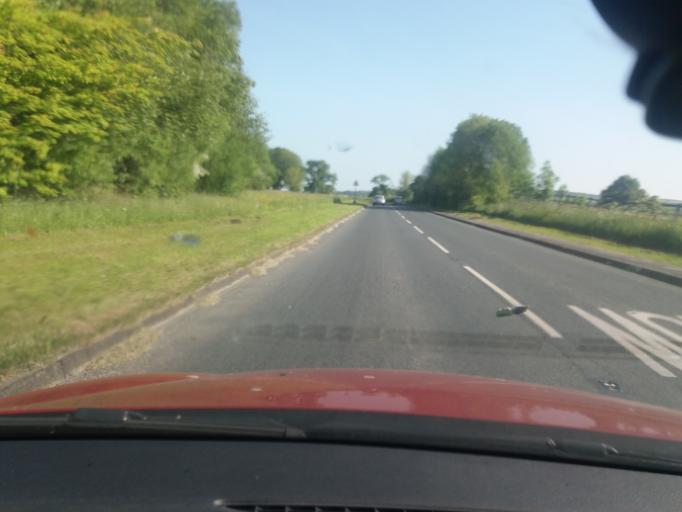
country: GB
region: England
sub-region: Borough of Wigan
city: Haigh
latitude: 53.6246
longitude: -2.5847
